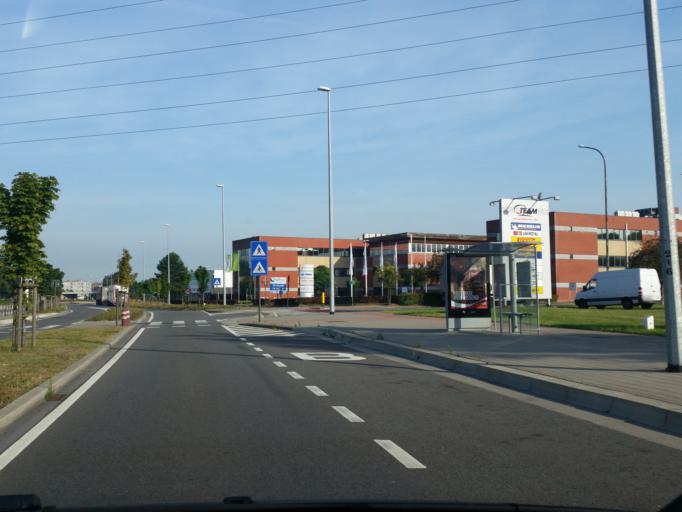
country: BE
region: Flanders
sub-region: Provincie Vlaams-Brabant
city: Machelen
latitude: 50.9233
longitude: 4.4419
